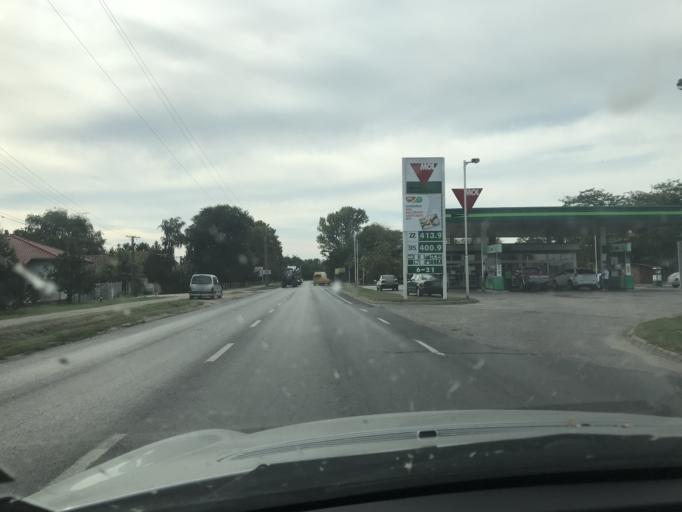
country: HU
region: Bacs-Kiskun
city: Kecel
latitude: 46.5198
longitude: 19.2422
